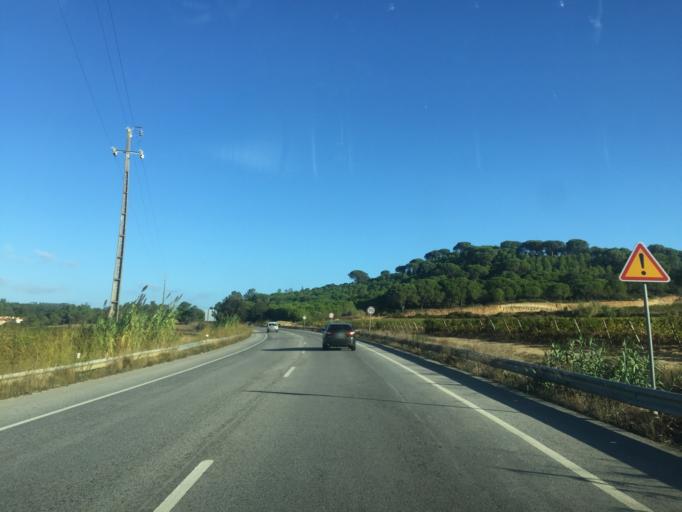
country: PT
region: Lisbon
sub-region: Azambuja
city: Alcoentre
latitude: 39.2151
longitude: -8.9535
